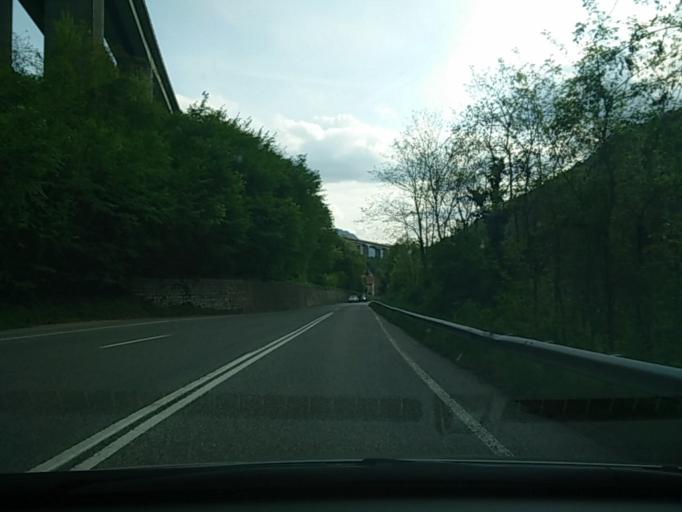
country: IT
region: Veneto
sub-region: Provincia di Treviso
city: Fregona
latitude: 46.0359
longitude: 12.3084
